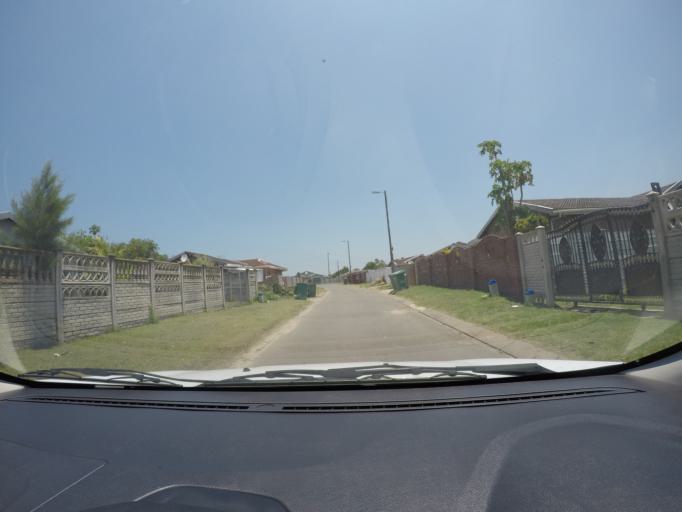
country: ZA
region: KwaZulu-Natal
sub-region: uThungulu District Municipality
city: eSikhawini
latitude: -28.8881
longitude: 31.8935
